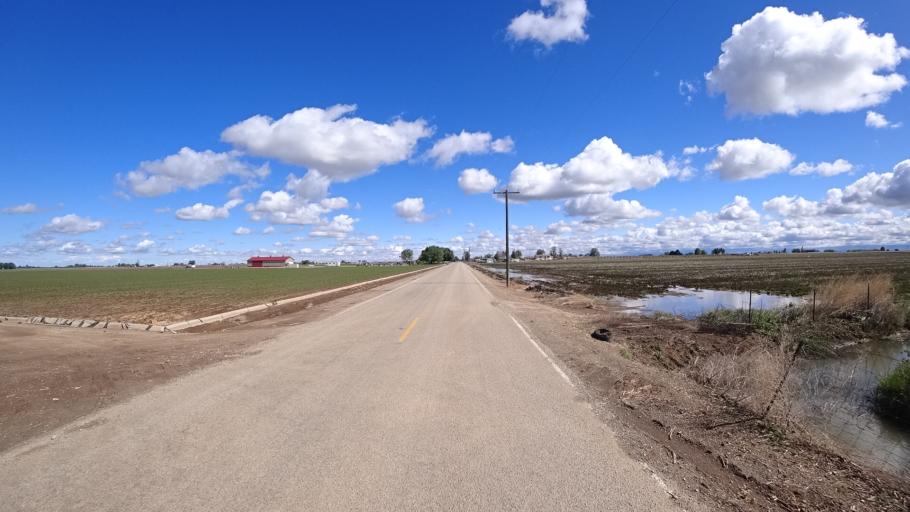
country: US
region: Idaho
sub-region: Ada County
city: Kuna
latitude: 43.4663
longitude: -116.4737
